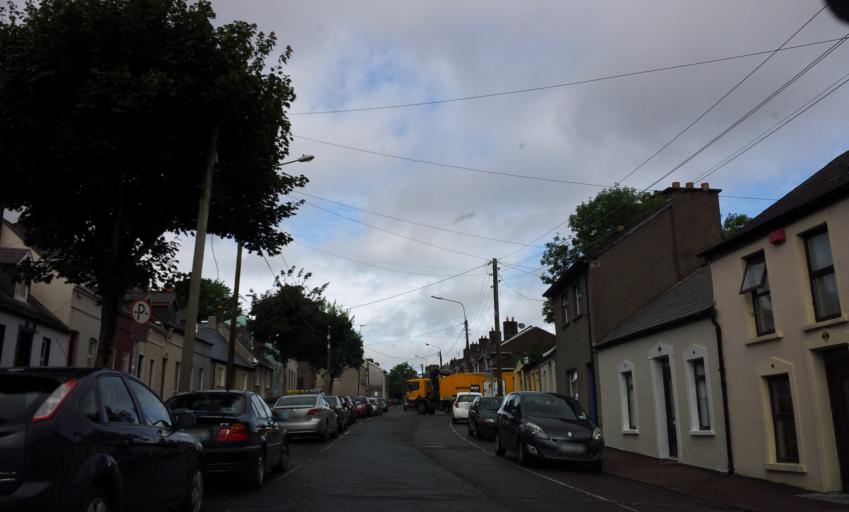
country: IE
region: Munster
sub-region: County Cork
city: Cork
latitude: 51.8904
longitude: -8.4703
